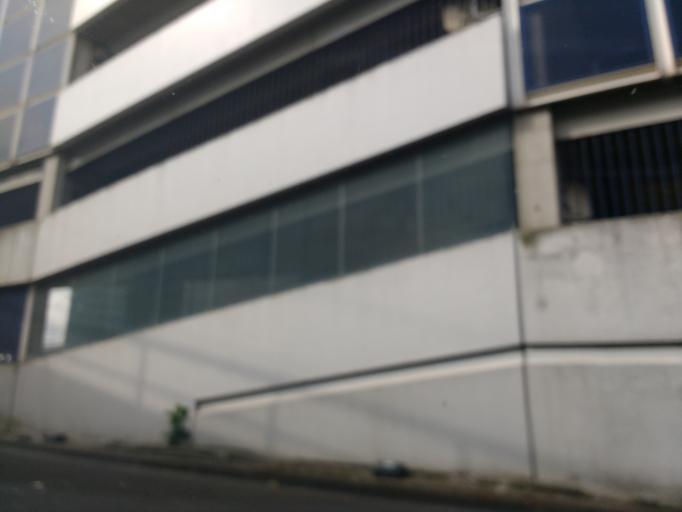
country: NL
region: North Holland
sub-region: Gemeente Zaanstad
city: Zaandam
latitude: 52.3913
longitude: 4.8383
